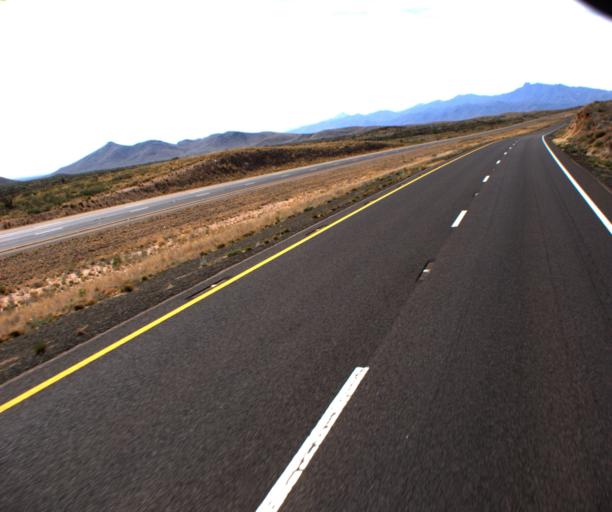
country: US
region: Arizona
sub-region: Cochise County
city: Willcox
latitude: 32.4529
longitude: -109.6645
